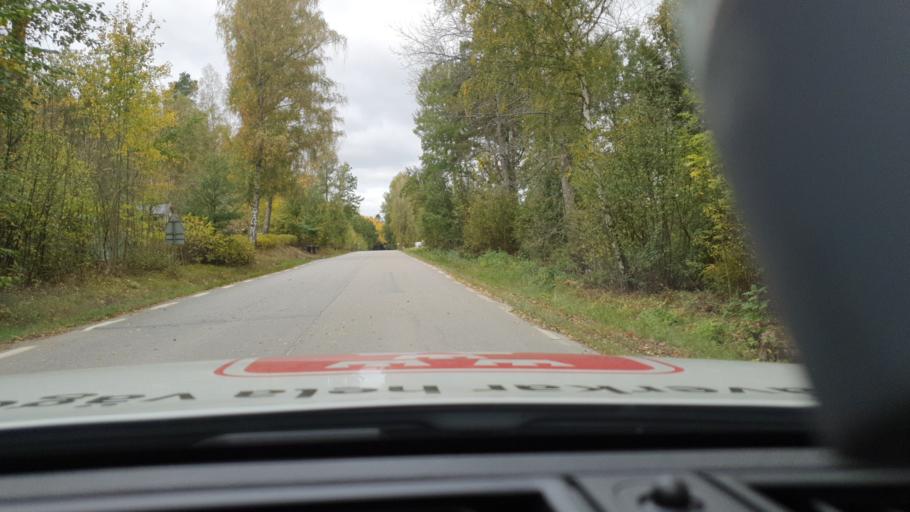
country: SE
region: Stockholm
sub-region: Upplands-Bro Kommun
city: Bro
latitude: 59.4973
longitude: 17.5689
